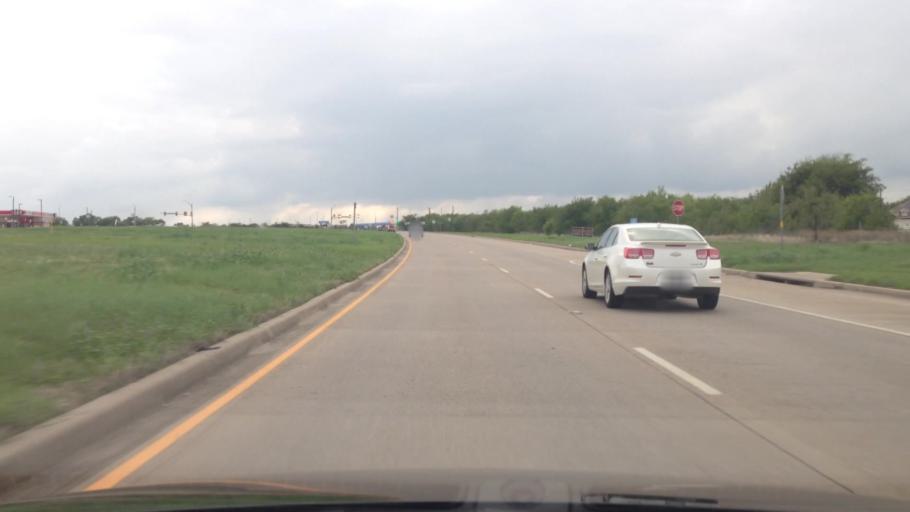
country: US
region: Texas
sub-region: Tarrant County
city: Crowley
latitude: 32.5778
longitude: -97.3310
